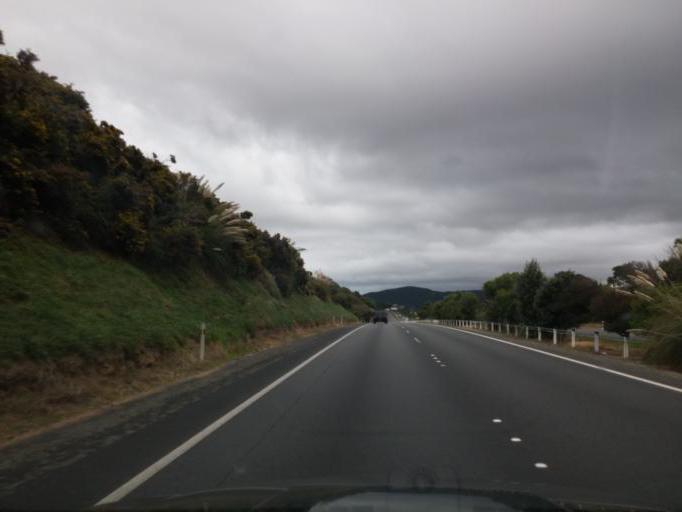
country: NZ
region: Wellington
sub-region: Porirua City
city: Porirua
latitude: -41.1601
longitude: 174.8366
